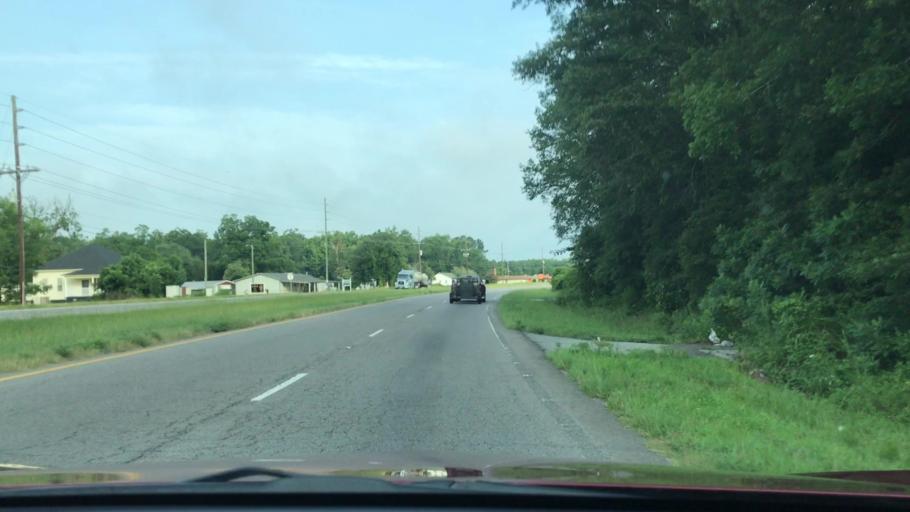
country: US
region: South Carolina
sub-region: Orangeburg County
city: Brookdale
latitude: 33.4706
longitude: -80.8032
